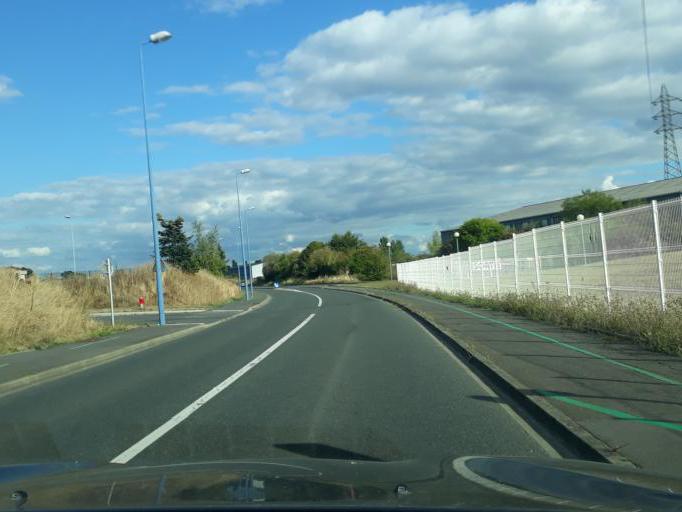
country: FR
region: Centre
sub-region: Departement du Loiret
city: Semoy
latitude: 47.9426
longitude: 1.9355
